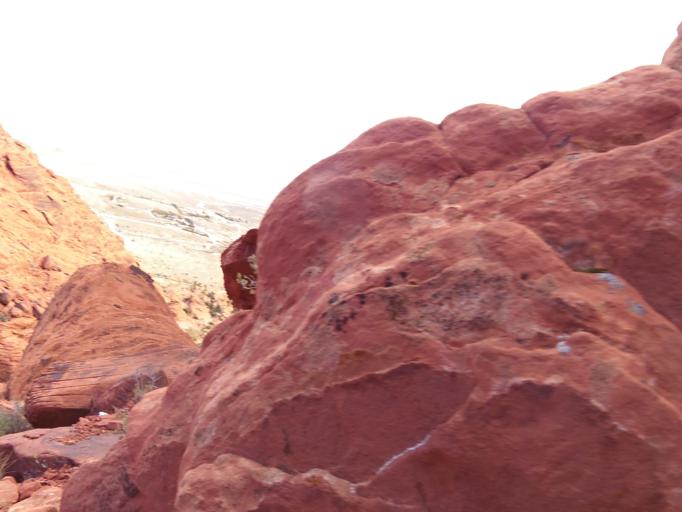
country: US
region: Nevada
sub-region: Clark County
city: Summerlin South
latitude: 36.1525
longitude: -115.4308
